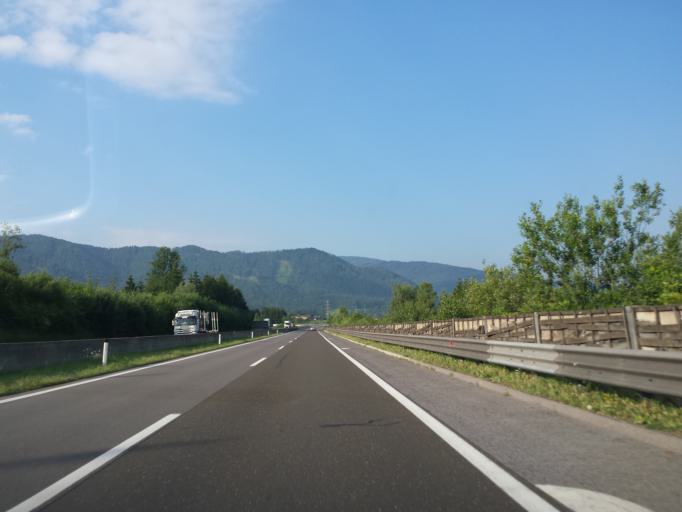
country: AT
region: Styria
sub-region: Politischer Bezirk Bruck-Muerzzuschlag
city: Krieglach
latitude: 47.5524
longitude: 15.5778
